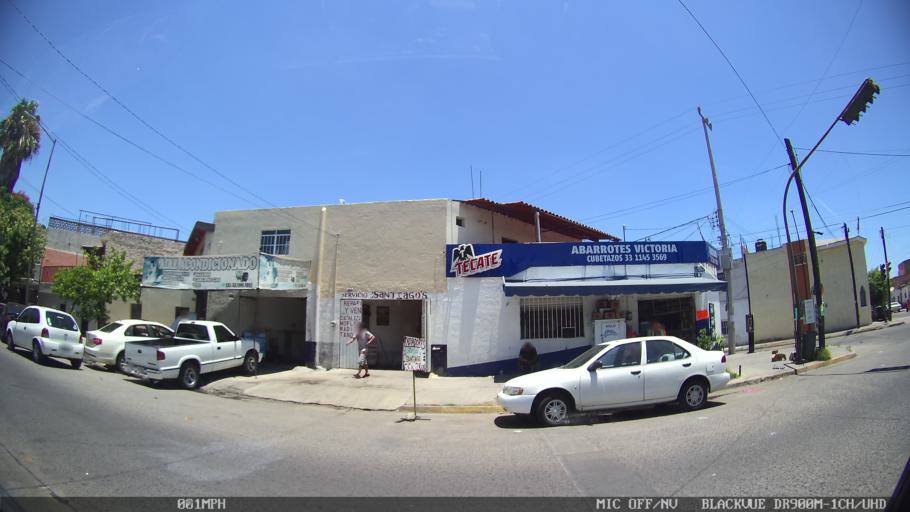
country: MX
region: Jalisco
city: Tlaquepaque
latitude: 20.6651
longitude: -103.2887
